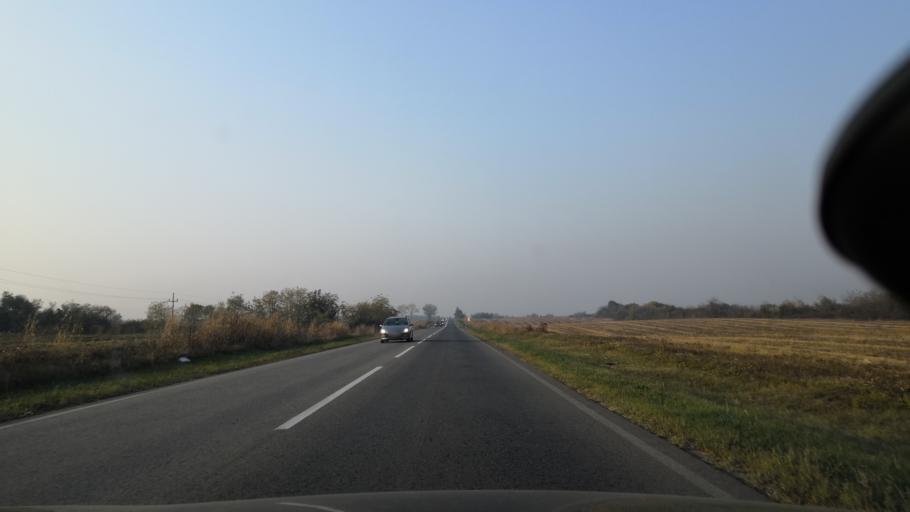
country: RS
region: Autonomna Pokrajina Vojvodina
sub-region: Sremski Okrug
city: Ingija
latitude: 45.0792
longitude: 20.0492
